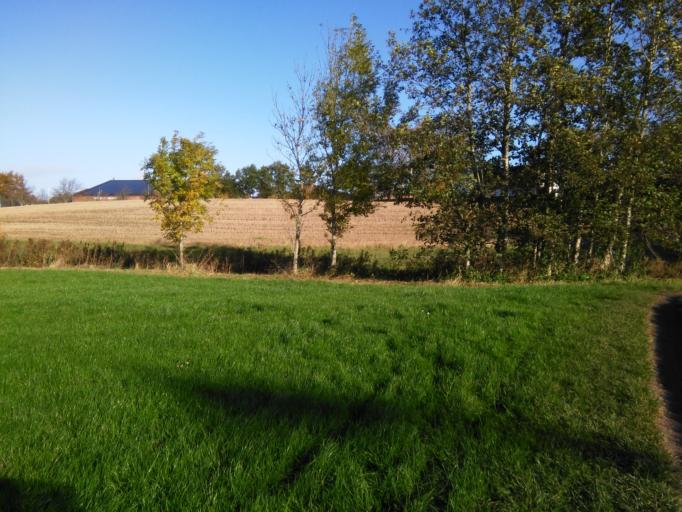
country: DK
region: Central Jutland
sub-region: Arhus Kommune
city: Marslet
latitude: 56.0670
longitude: 10.1558
